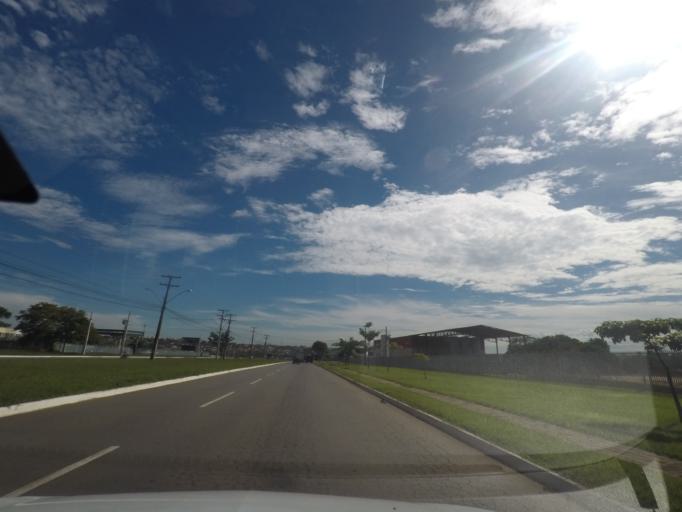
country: BR
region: Goias
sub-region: Aparecida De Goiania
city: Aparecida de Goiania
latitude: -16.7906
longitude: -49.2523
